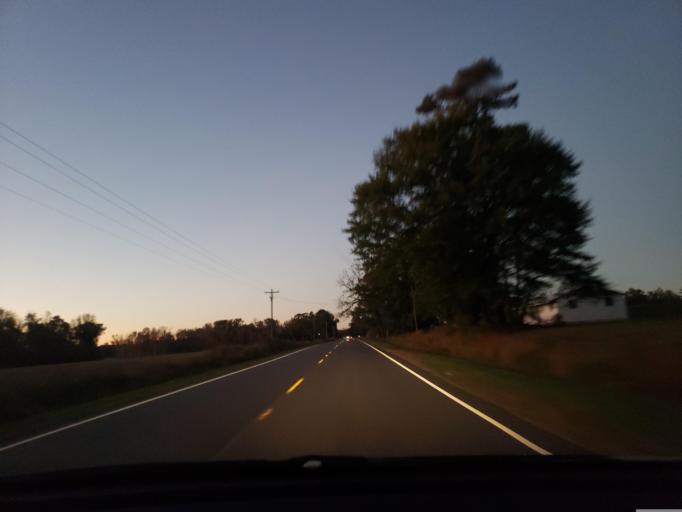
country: US
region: North Carolina
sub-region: Duplin County
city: Kenansville
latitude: 34.9315
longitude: -77.9402
